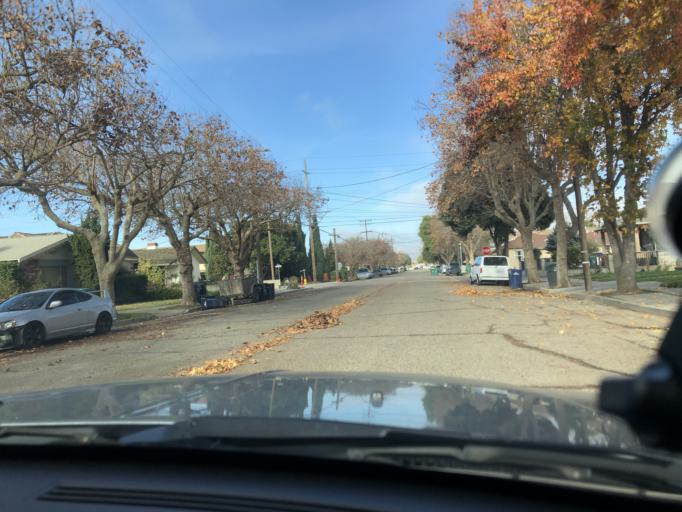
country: US
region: California
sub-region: Monterey County
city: King City
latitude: 36.2146
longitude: -121.1296
